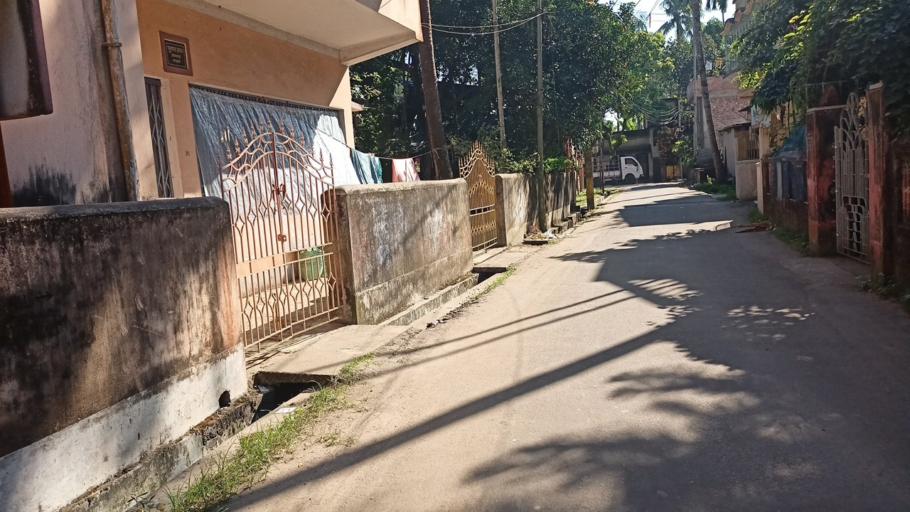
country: IN
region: West Bengal
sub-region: North 24 Parganas
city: Bangaon
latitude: 23.0510
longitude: 88.8242
